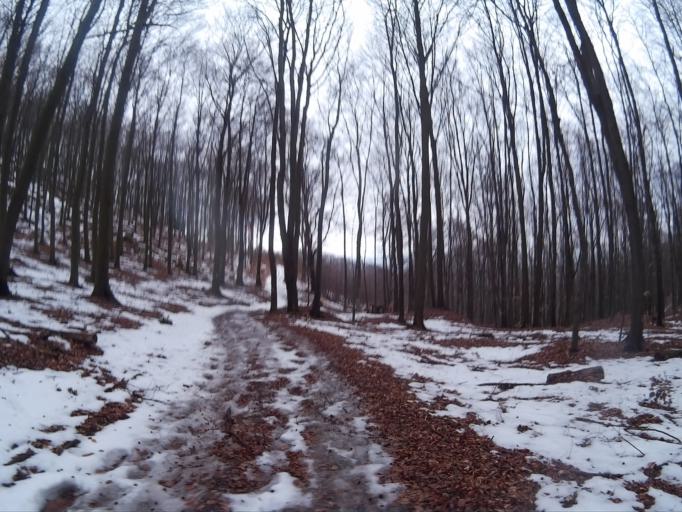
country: HU
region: Heves
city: Belapatfalva
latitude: 48.0463
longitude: 20.3943
